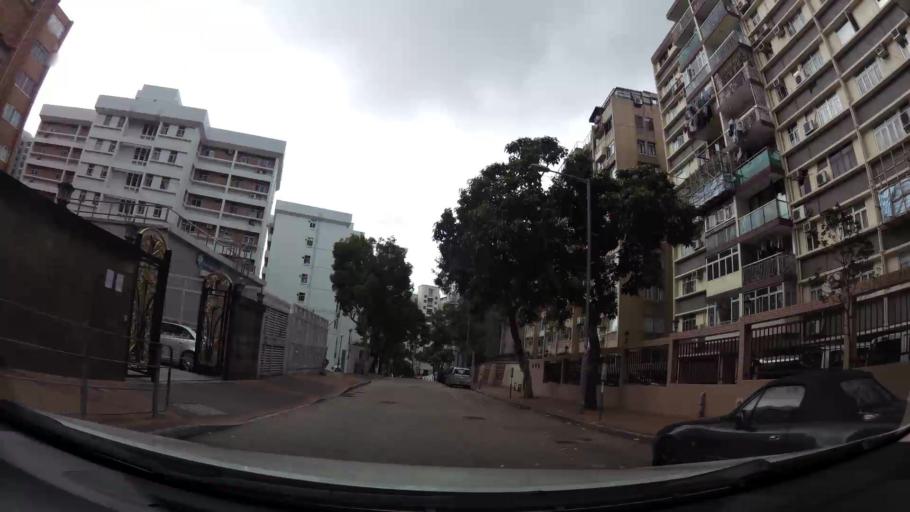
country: HK
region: Wong Tai Sin
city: Wong Tai Sin
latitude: 22.3417
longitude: 114.1832
